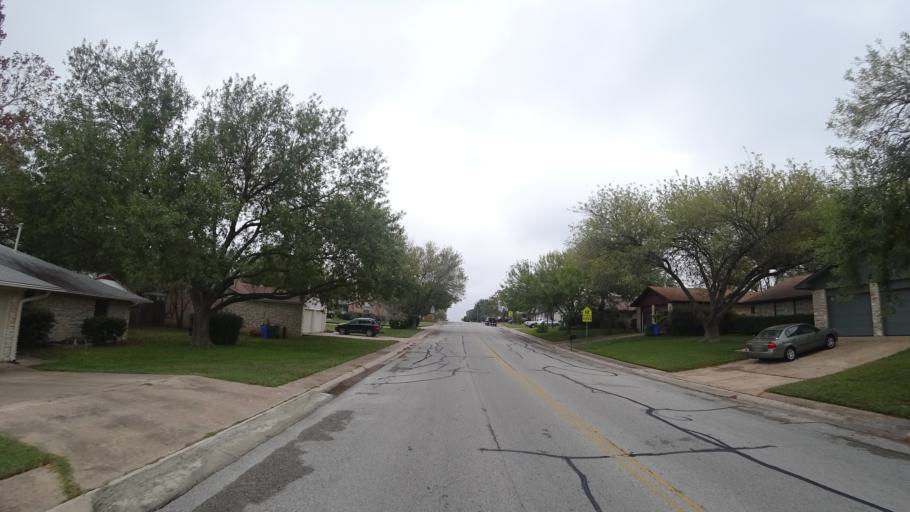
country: US
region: Texas
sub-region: Travis County
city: Pflugerville
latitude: 30.4299
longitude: -97.6125
